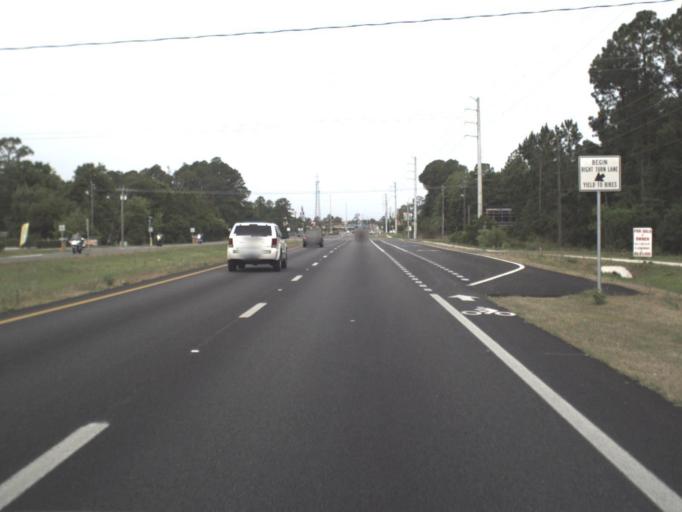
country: US
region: Florida
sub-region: Saint Johns County
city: Saint Augustine
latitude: 29.9153
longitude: -81.4013
